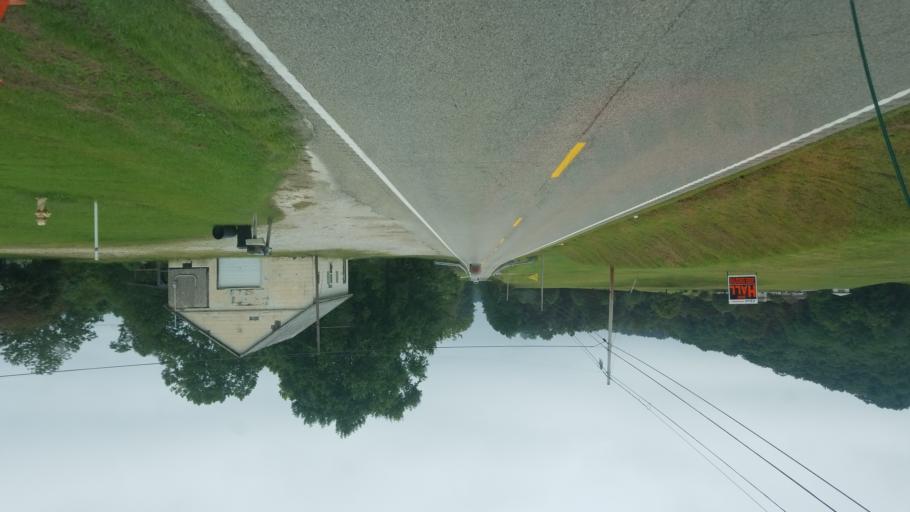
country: US
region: Kentucky
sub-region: Rowan County
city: Morehead
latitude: 38.2217
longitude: -83.4691
